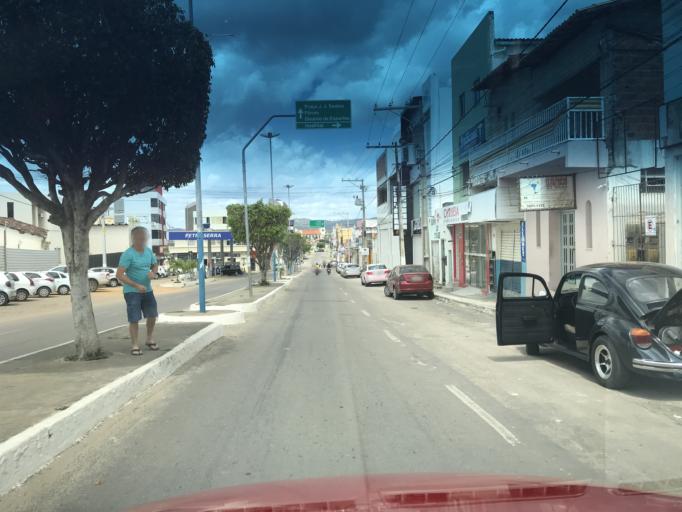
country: BR
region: Bahia
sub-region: Itaberaba
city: Itaberaba
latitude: -12.5295
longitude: -40.3077
